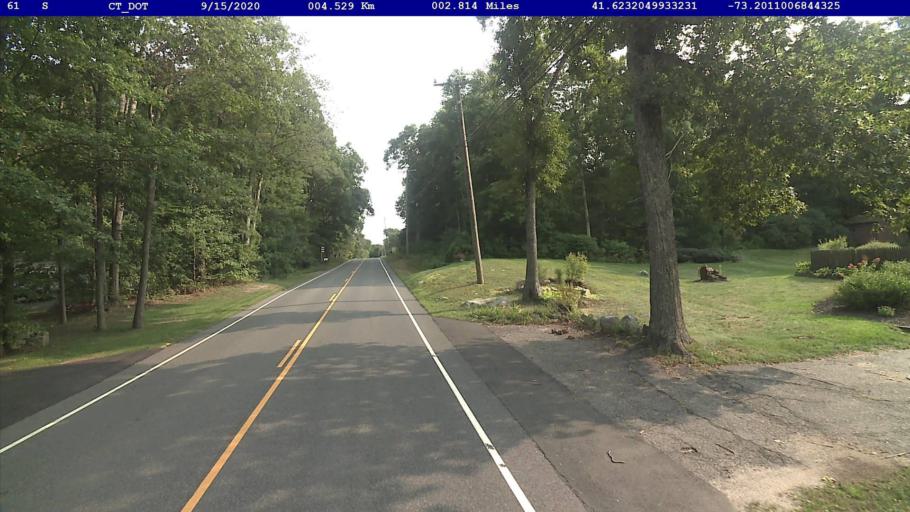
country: US
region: Connecticut
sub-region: Litchfield County
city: Bethlehem Village
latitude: 41.6232
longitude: -73.2011
